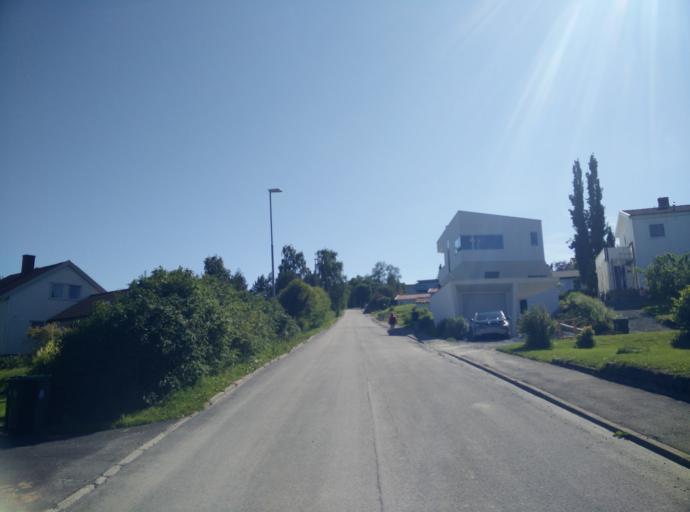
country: NO
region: Sor-Trondelag
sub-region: Trondheim
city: Trondheim
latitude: 63.4108
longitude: 10.3737
